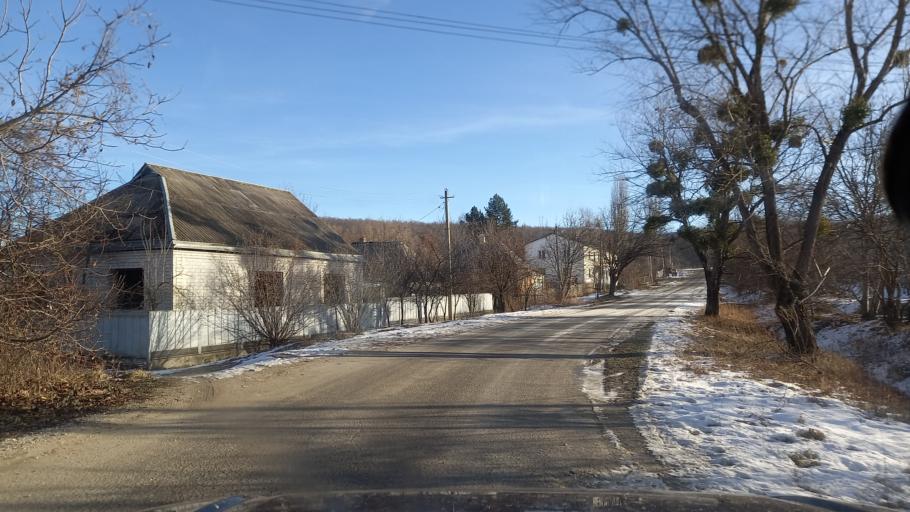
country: RU
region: Adygeya
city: Kamennomostskiy
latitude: 44.2953
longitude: 40.1881
